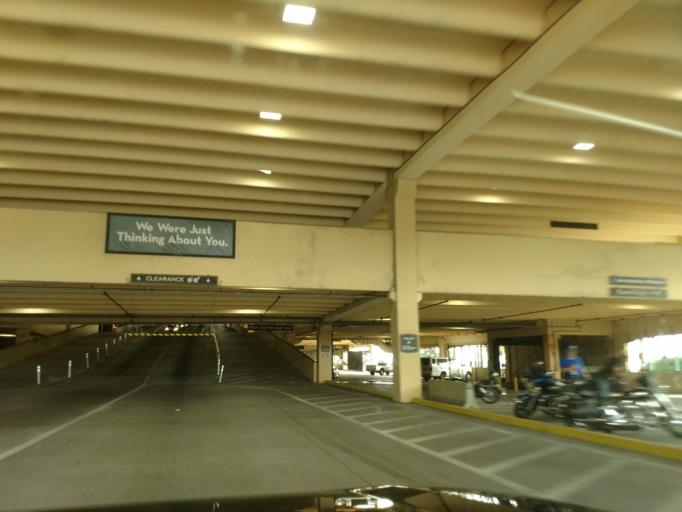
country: US
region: Mississippi
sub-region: Harrison County
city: Biloxi
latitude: 30.3938
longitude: -88.8936
